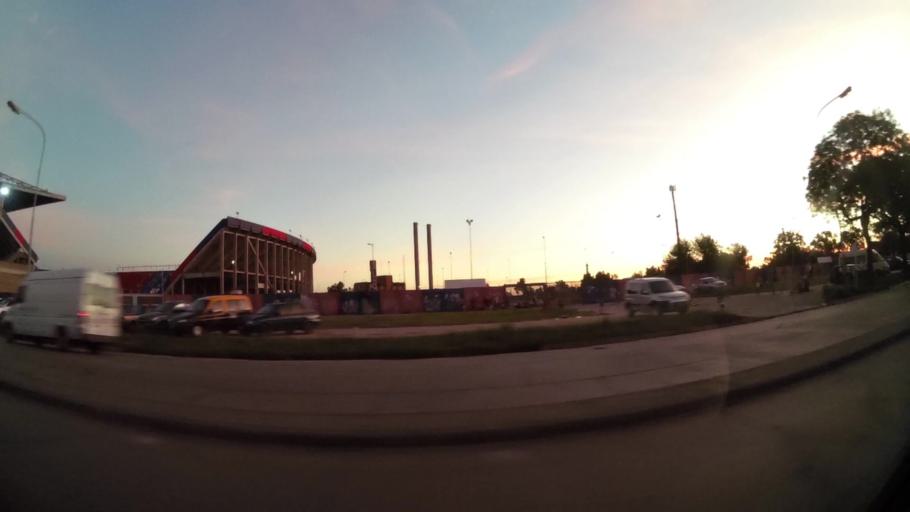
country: AR
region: Buenos Aires F.D.
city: Villa Lugano
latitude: -34.6508
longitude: -58.4419
